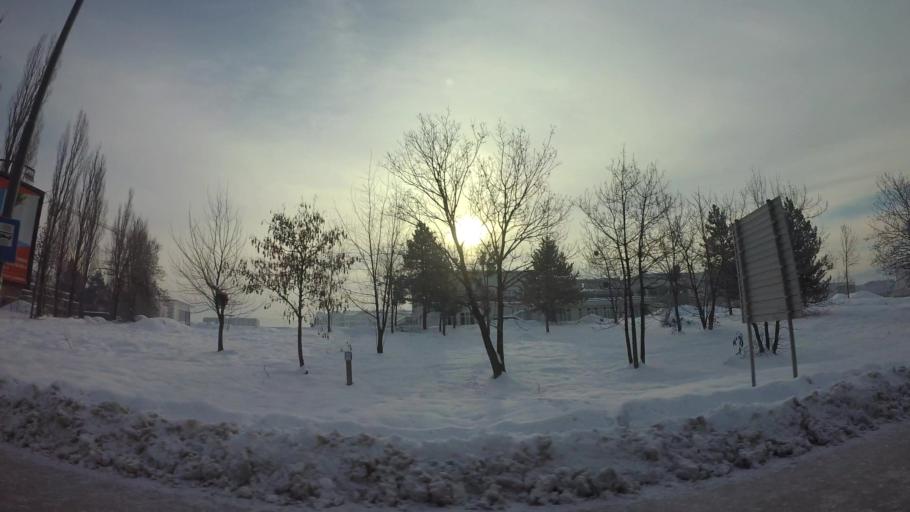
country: BA
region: Federation of Bosnia and Herzegovina
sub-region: Kanton Sarajevo
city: Sarajevo
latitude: 43.8231
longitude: 18.3619
